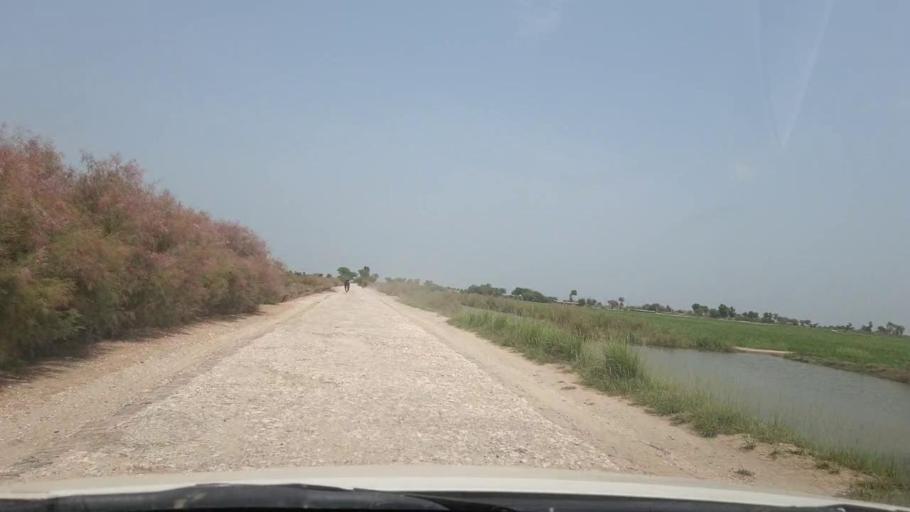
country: PK
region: Sindh
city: Rustam jo Goth
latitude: 28.0396
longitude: 68.8144
